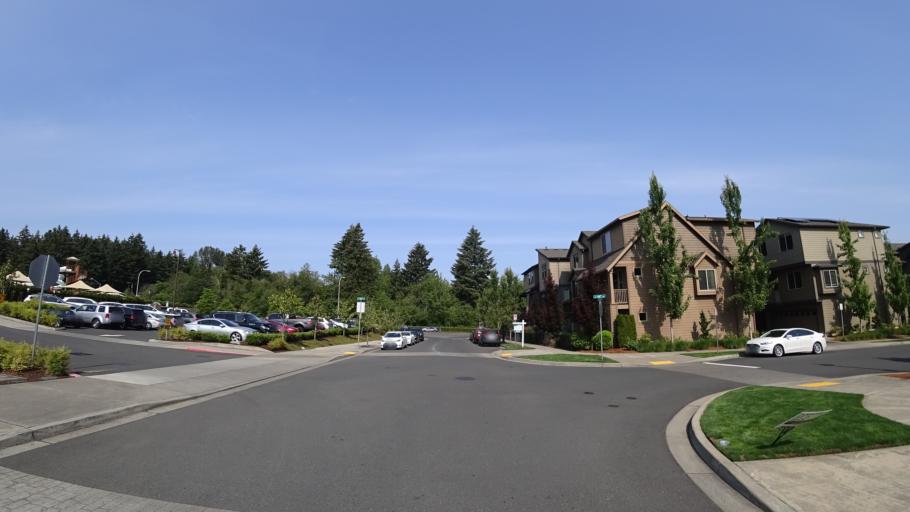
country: US
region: Oregon
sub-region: Washington County
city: Cedar Mill
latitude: 45.5048
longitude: -122.8250
